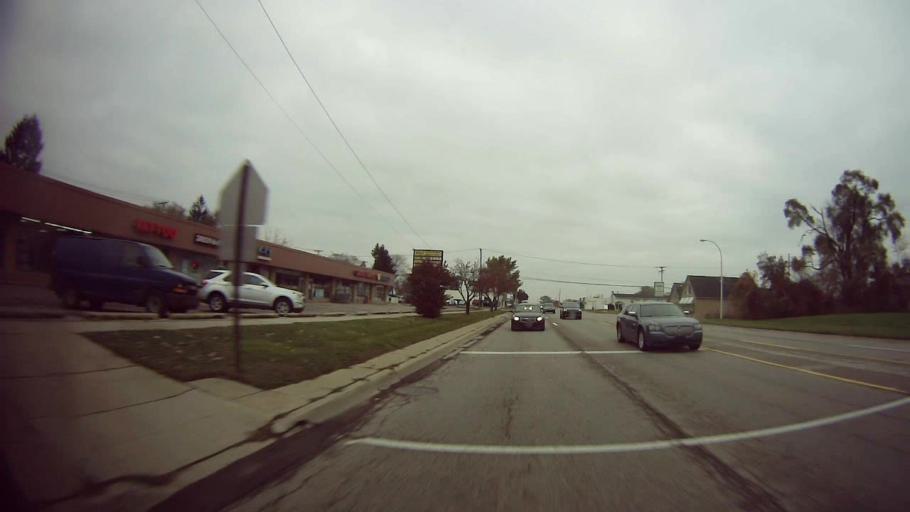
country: US
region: Michigan
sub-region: Oakland County
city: Madison Heights
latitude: 42.5169
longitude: -83.1064
